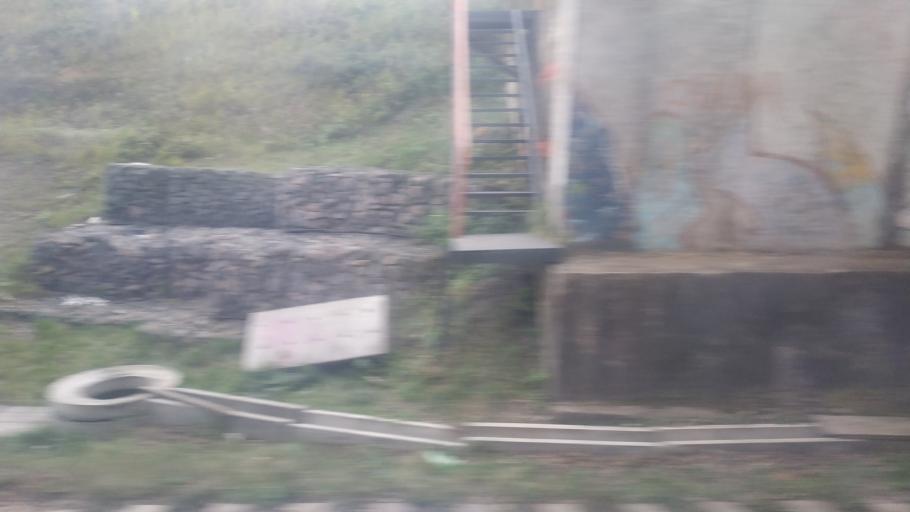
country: RU
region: Moskovskaya
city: Ozherel'ye
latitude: 54.8115
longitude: 38.2688
